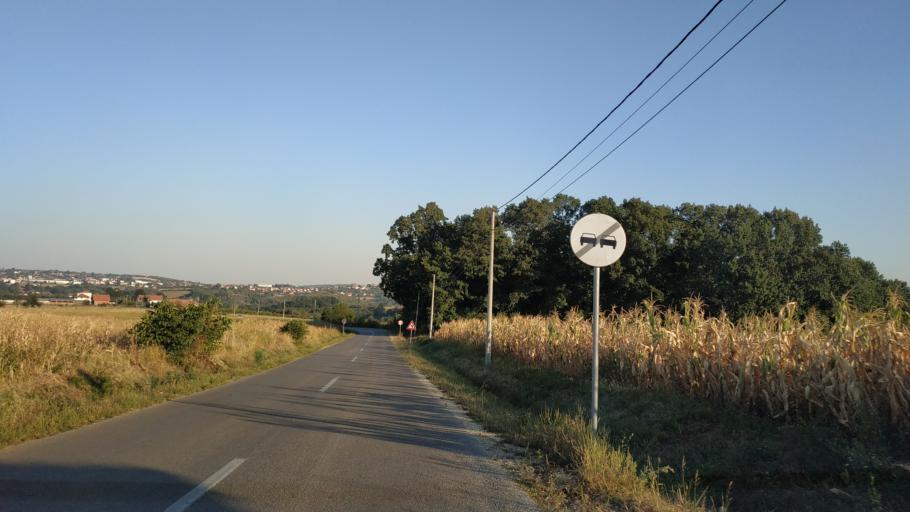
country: RS
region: Central Serbia
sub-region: Sumadijski Okrug
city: Topola
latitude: 44.2692
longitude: 20.6544
